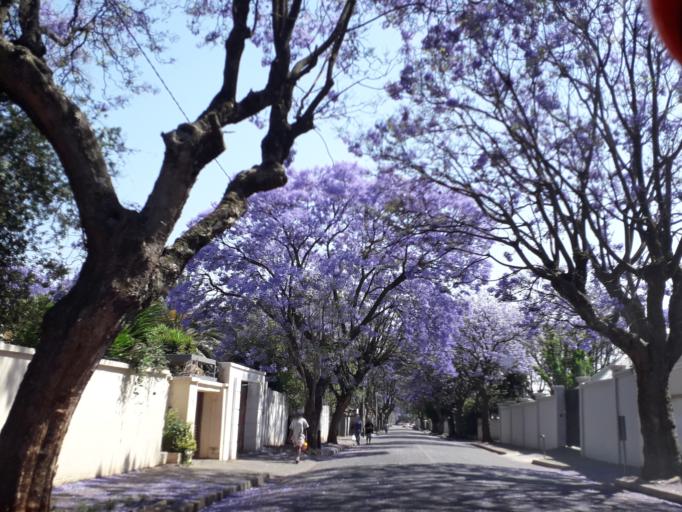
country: ZA
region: Gauteng
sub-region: City of Johannesburg Metropolitan Municipality
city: Johannesburg
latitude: -26.1615
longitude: 28.0867
